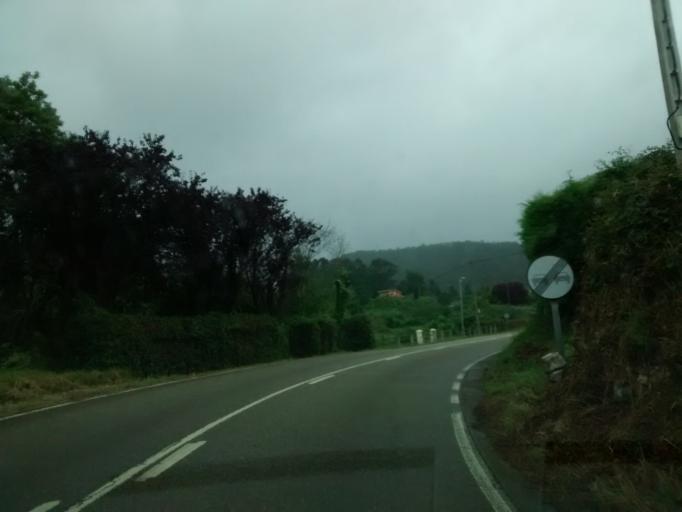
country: ES
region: Asturias
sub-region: Province of Asturias
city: Villaviciosa
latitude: 43.5274
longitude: -5.3739
